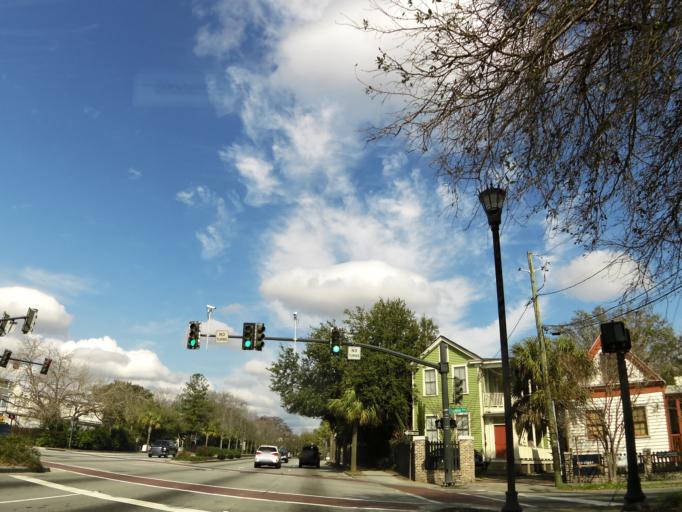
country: US
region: South Carolina
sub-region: Charleston County
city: Charleston
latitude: 32.7913
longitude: -79.9498
